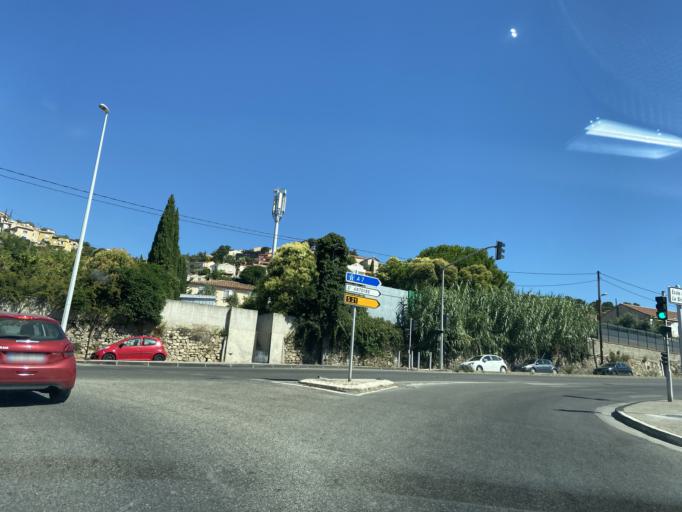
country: FR
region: Provence-Alpes-Cote d'Azur
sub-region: Departement des Bouches-du-Rhone
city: Marseille 15
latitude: 43.3701
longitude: 5.3464
